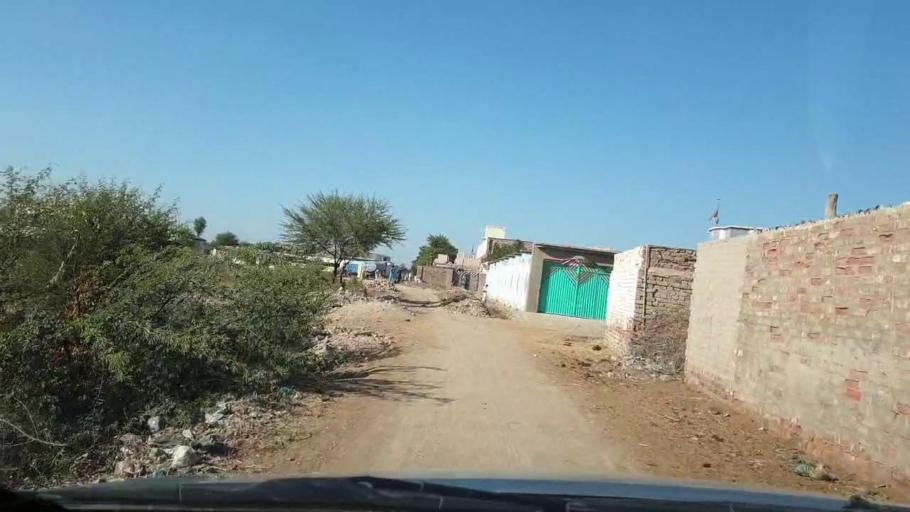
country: PK
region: Sindh
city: Berani
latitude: 25.8191
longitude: 68.9420
